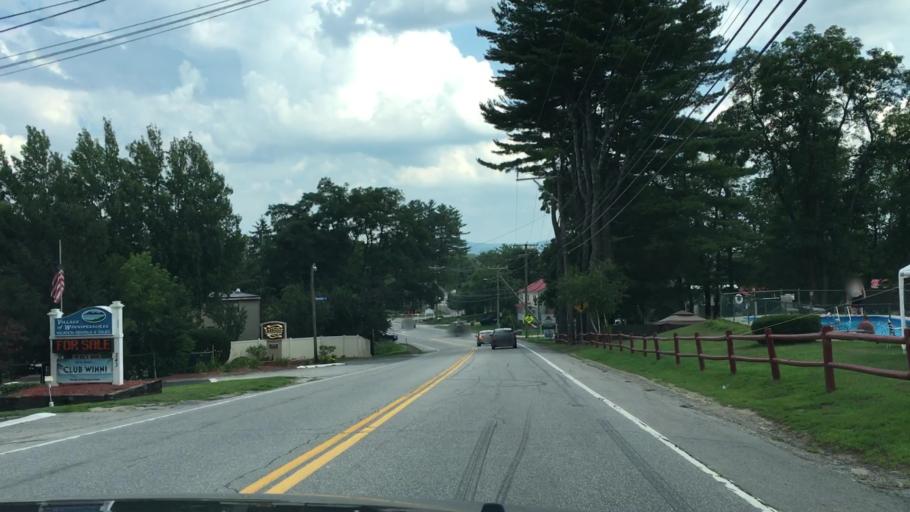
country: US
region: New Hampshire
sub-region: Belknap County
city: Meredith
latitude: 43.6068
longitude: -71.4662
